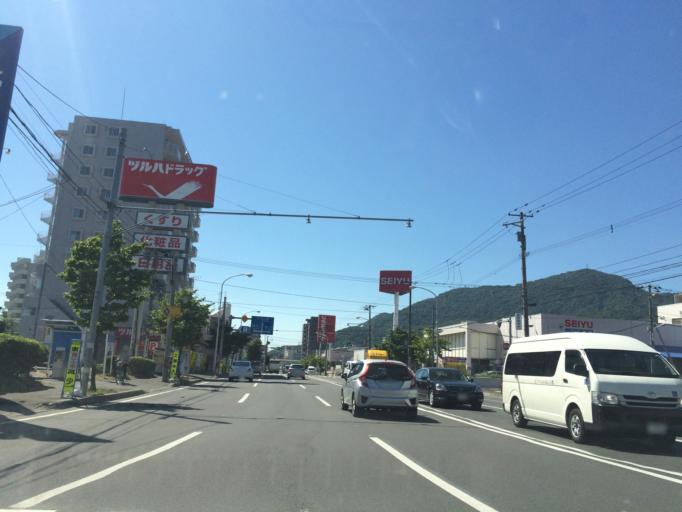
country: JP
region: Hokkaido
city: Sapporo
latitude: 43.0471
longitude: 141.3226
